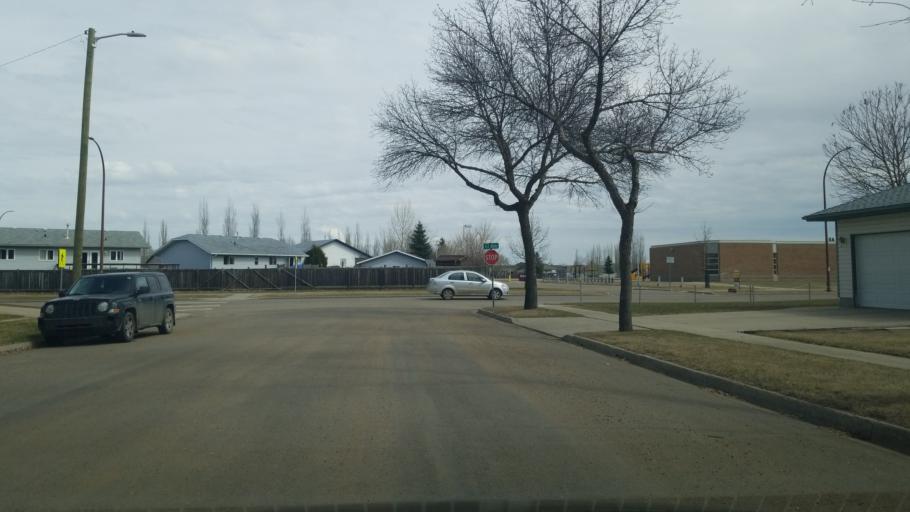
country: CA
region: Saskatchewan
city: Lloydminster
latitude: 53.2725
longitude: -109.9981
